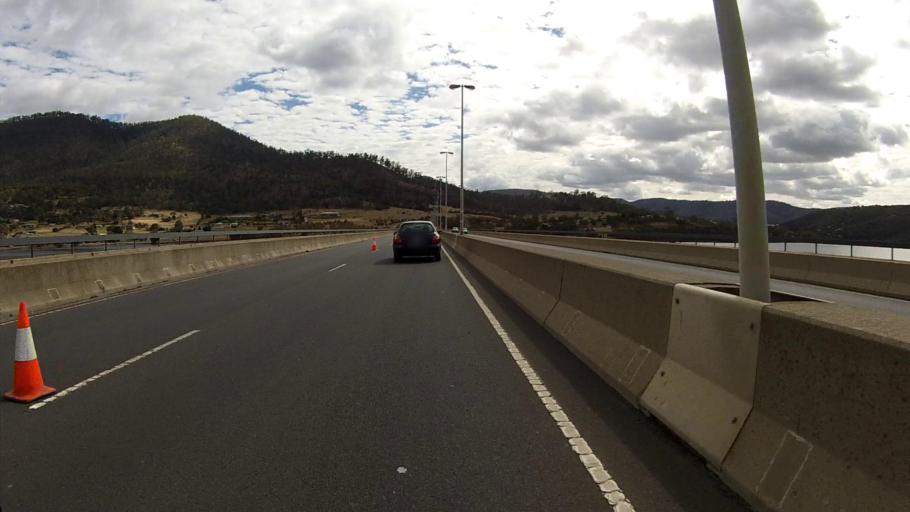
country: AU
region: Tasmania
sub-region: Glenorchy
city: Goodwood
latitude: -42.8184
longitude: 147.3062
